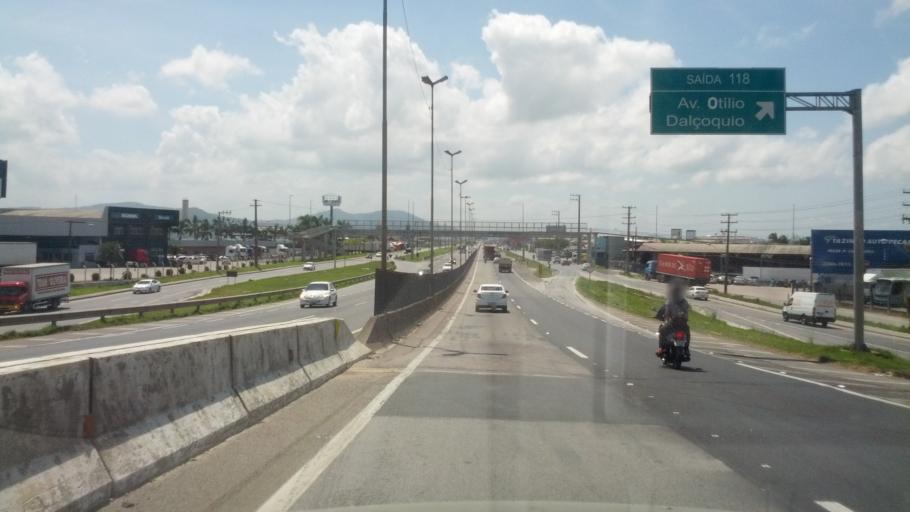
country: BR
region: Santa Catarina
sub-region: Itajai
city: Itajai
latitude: -26.8895
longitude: -48.7216
